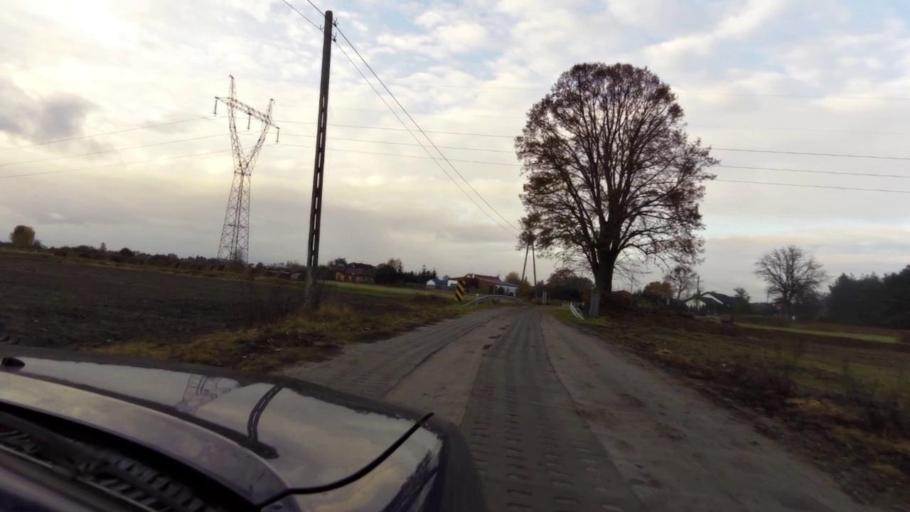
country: PL
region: West Pomeranian Voivodeship
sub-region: Powiat goleniowski
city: Goleniow
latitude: 53.5842
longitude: 14.7618
